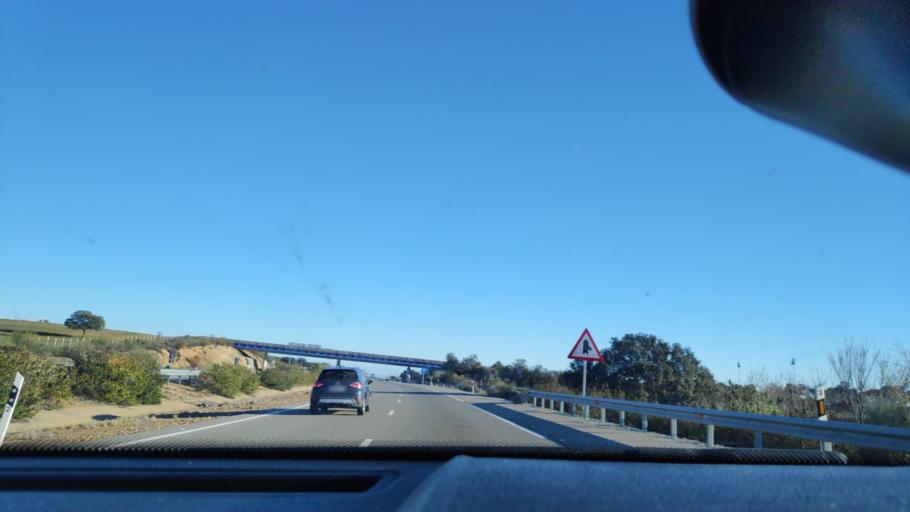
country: ES
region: Andalusia
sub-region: Provincia de Sevilla
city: Gerena
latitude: 37.6272
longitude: -6.1438
